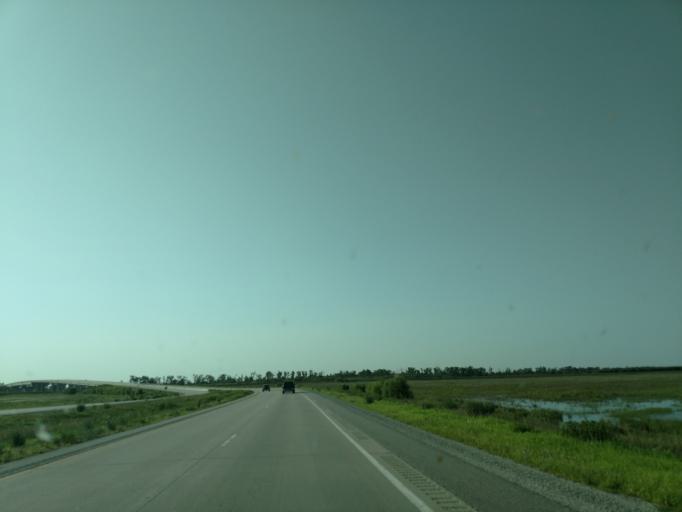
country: US
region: Nebraska
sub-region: Cass County
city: Plattsmouth
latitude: 41.0607
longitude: -95.8687
